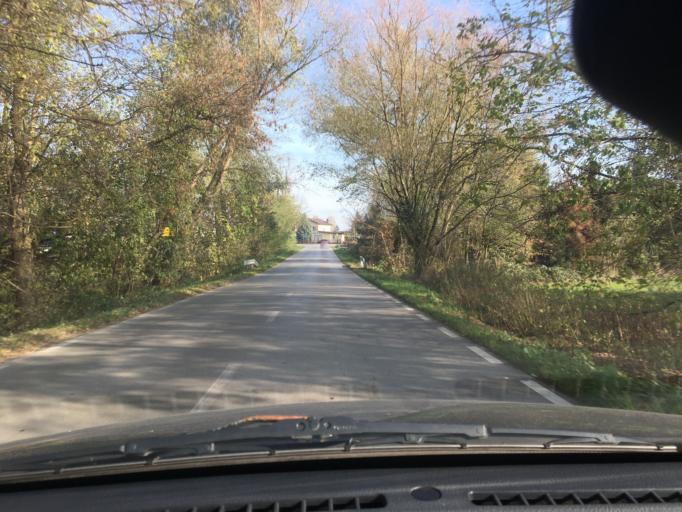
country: PL
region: Masovian Voivodeship
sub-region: Powiat plocki
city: Bodzanow
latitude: 52.4918
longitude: 20.0288
